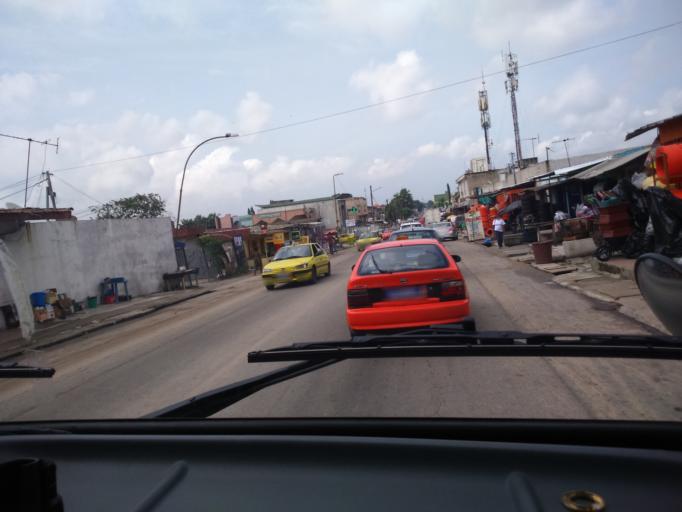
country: CI
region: Lagunes
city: Abobo
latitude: 5.3679
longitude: -3.9798
